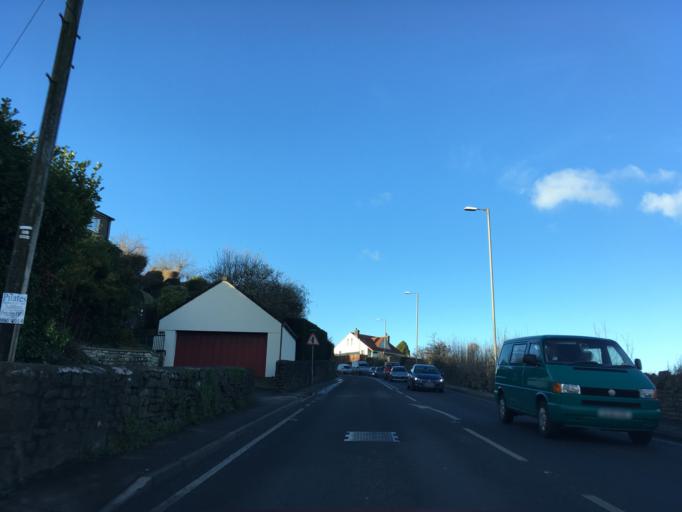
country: GB
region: England
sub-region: Bath and North East Somerset
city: Saltford
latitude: 51.3997
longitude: -2.4516
